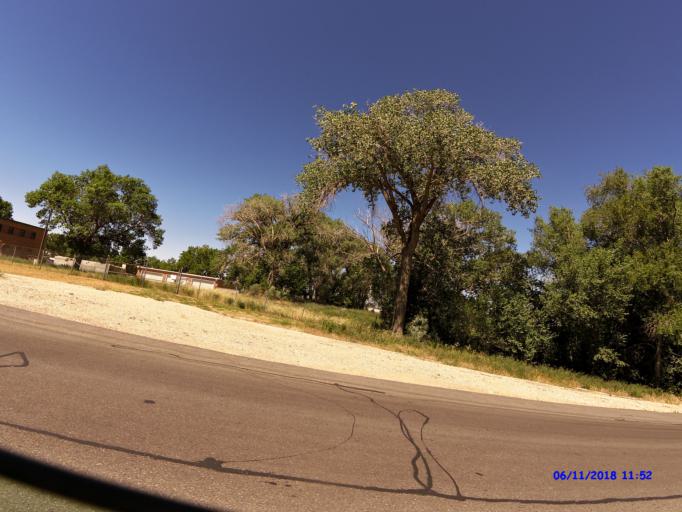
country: US
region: Utah
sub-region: Weber County
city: Ogden
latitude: 41.2336
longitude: -111.9535
